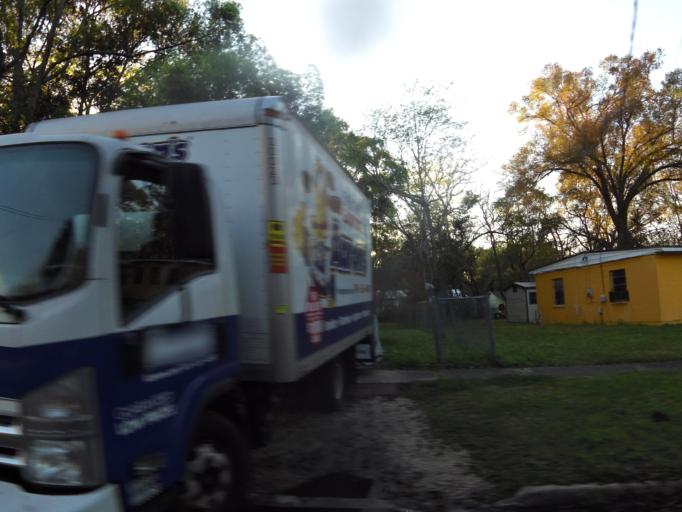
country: US
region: Florida
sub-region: Duval County
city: Jacksonville
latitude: 30.3390
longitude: -81.7132
